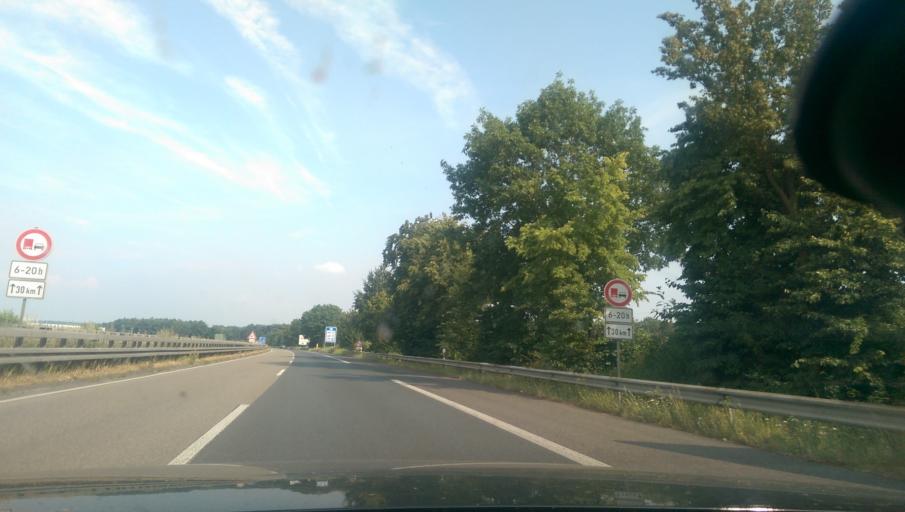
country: NL
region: Limburg
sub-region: Gemeente Venlo
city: Venlo
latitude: 51.3818
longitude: 6.2236
